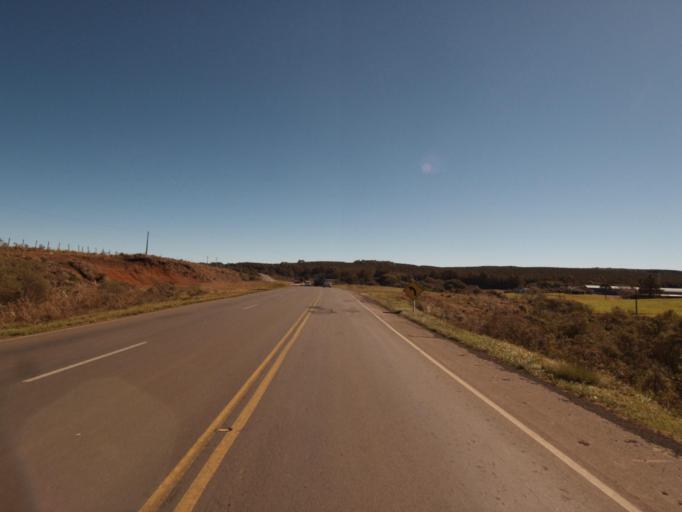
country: BR
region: Santa Catarina
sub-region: Concordia
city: Concordia
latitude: -26.9197
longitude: -51.8848
